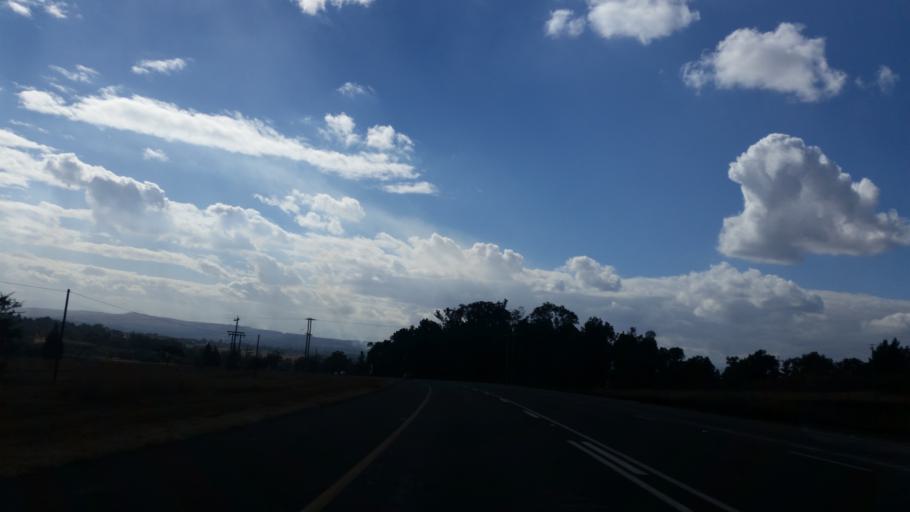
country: ZA
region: KwaZulu-Natal
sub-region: Amajuba District Municipality
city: Newcastle
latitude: -27.8019
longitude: 29.9564
